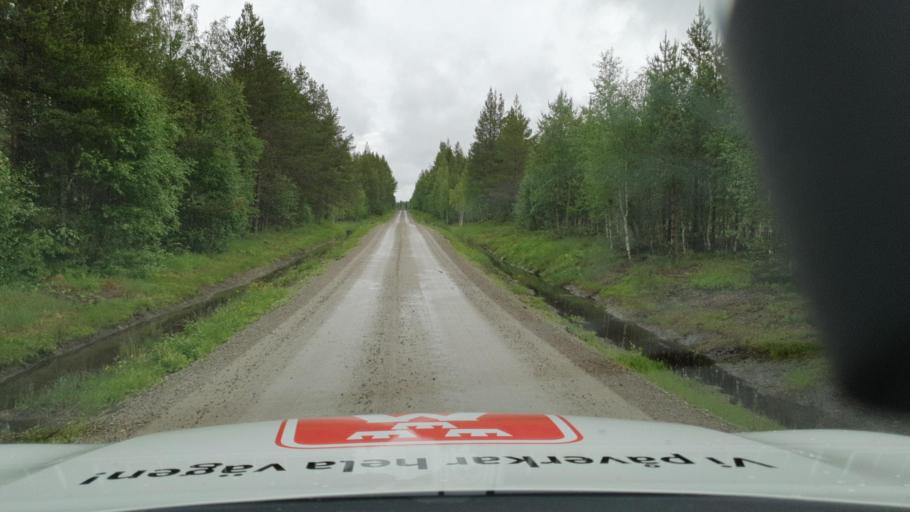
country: SE
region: Vaesterbotten
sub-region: Dorotea Kommun
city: Dorotea
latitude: 64.0023
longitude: 16.7988
